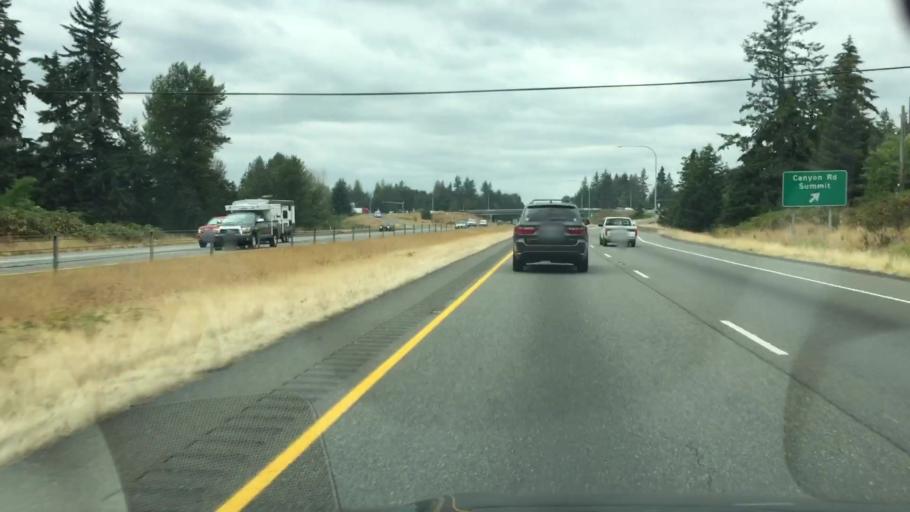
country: US
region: Washington
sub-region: Pierce County
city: Summit
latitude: 47.1579
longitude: -122.3504
